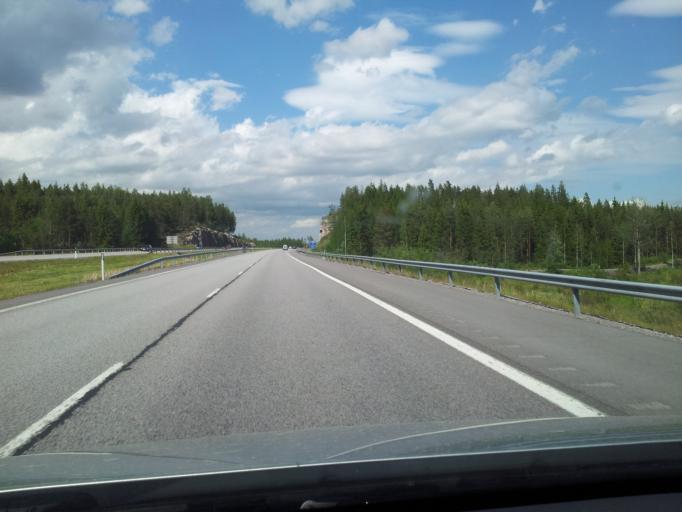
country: FI
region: Uusimaa
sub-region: Loviisa
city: Perna
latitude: 60.4710
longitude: 25.8602
